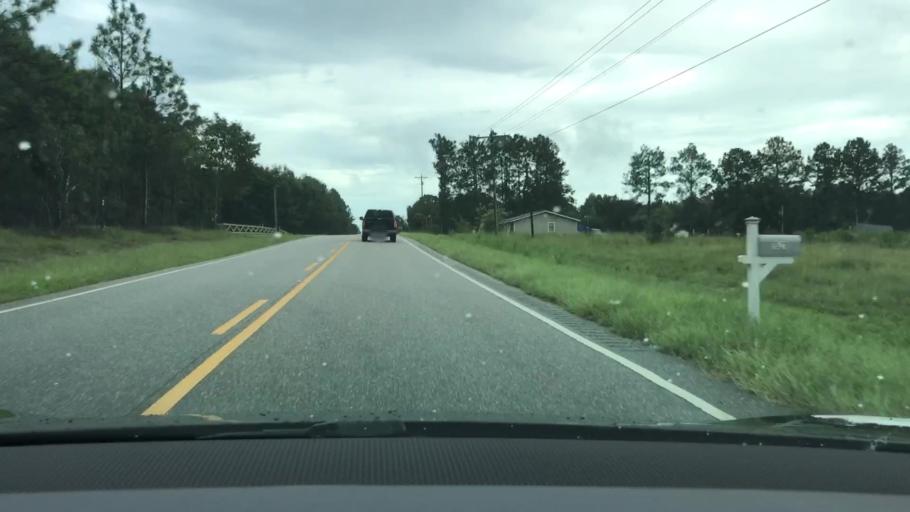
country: US
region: Alabama
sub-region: Geneva County
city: Samson
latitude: 31.0927
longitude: -86.1105
